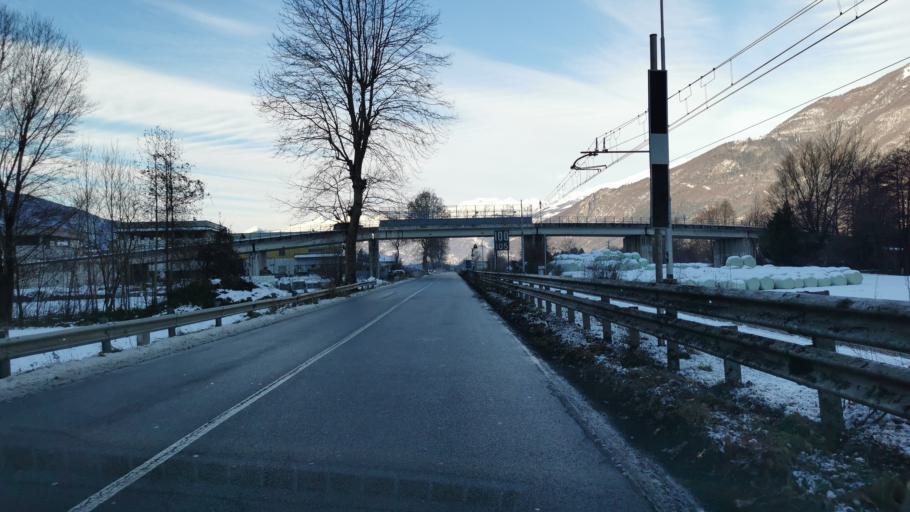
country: IT
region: Lombardy
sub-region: Provincia di Sondrio
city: Rogolo
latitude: 46.1370
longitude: 9.5050
